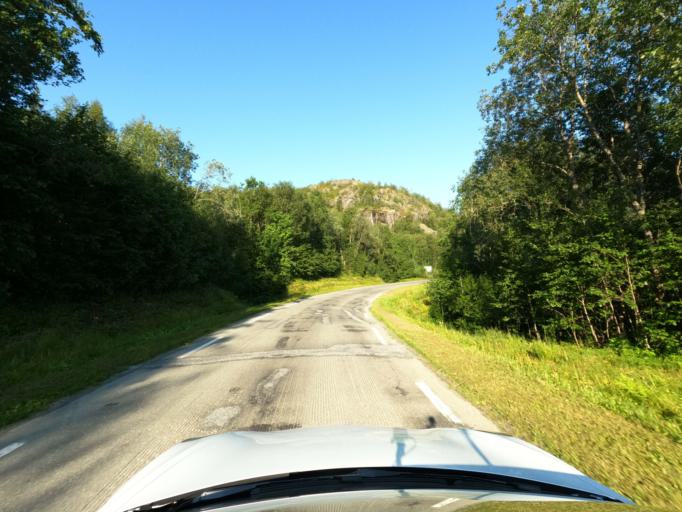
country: NO
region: Nordland
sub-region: Narvik
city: Bjerkvik
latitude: 68.5536
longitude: 17.5720
